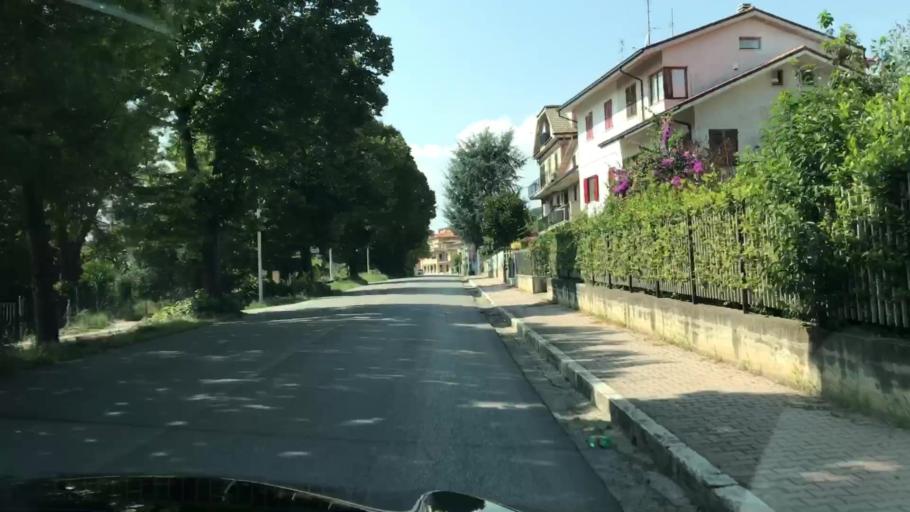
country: IT
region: The Marches
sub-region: Provincia di Ascoli Piceno
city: Pagliare
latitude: 42.8746
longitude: 13.7716
